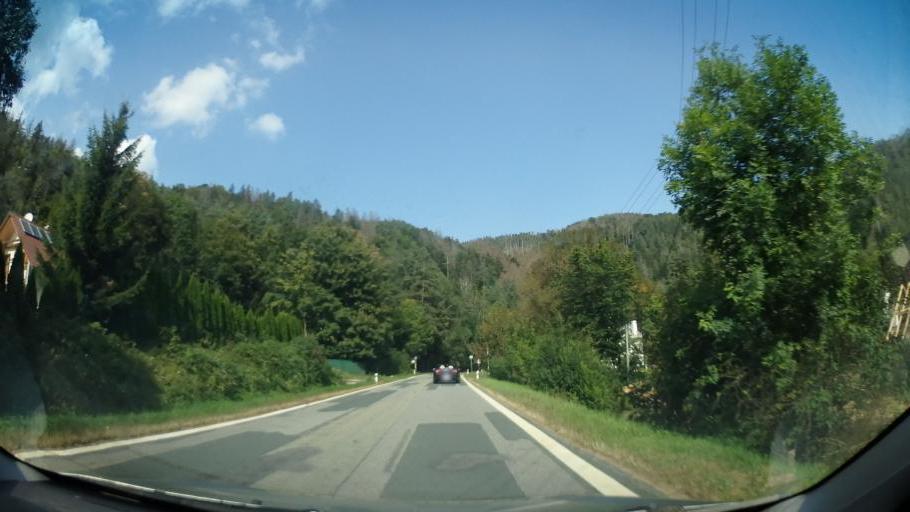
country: CZ
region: Vysocina
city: Bystrice nad Pernstejnem
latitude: 49.5479
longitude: 16.3382
